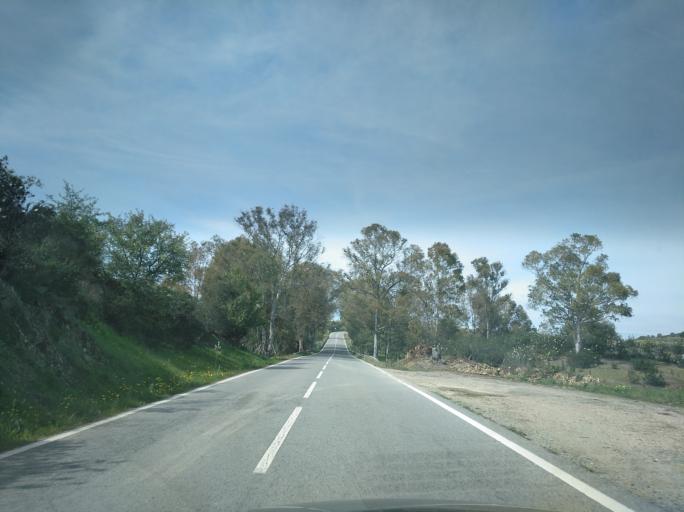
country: PT
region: Beja
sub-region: Mertola
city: Mertola
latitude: 37.5535
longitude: -7.6525
